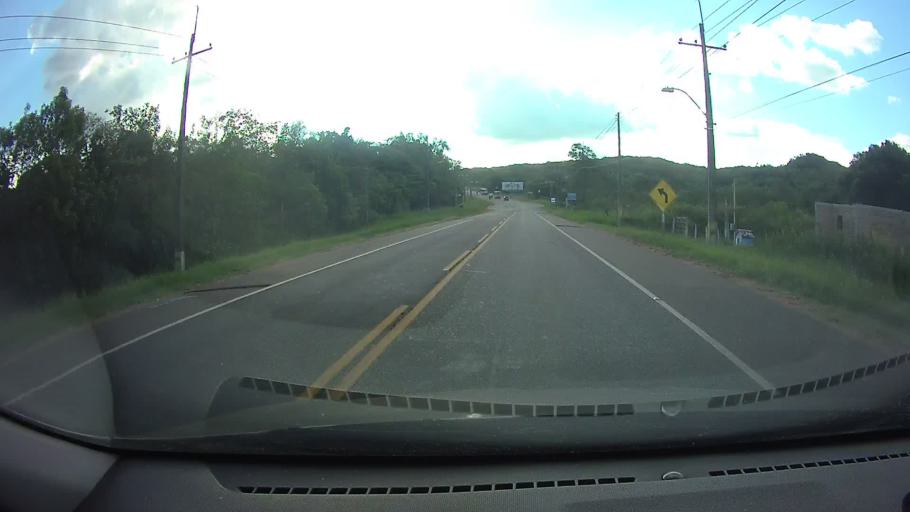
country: PY
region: Cordillera
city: Caacupe
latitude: -25.3889
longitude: -57.0826
